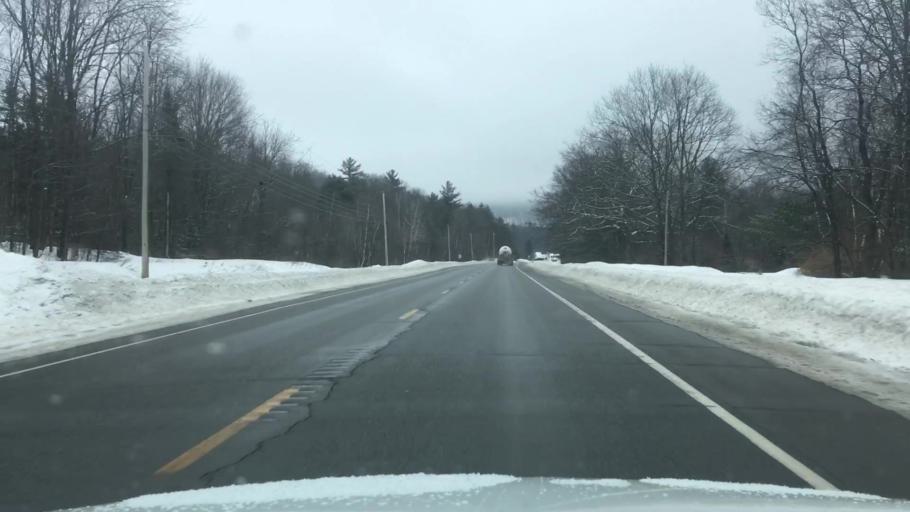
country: US
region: Maine
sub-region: Oxford County
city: Peru
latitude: 44.5798
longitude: -70.3326
